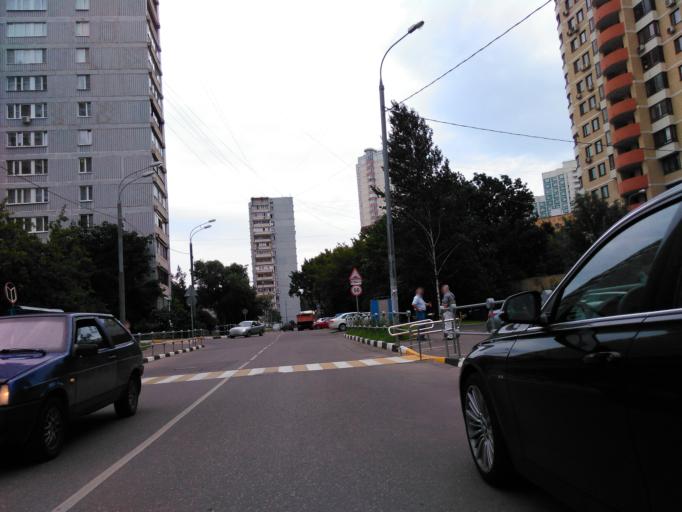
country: RU
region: Moscow
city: Troparevo
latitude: 55.6648
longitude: 37.5166
